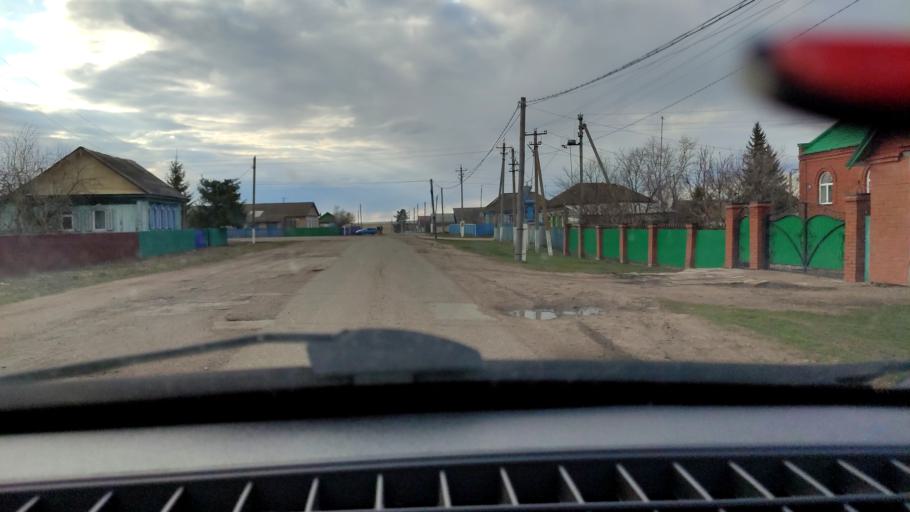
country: RU
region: Bashkortostan
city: Karmaskaly
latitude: 54.3357
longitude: 56.0002
